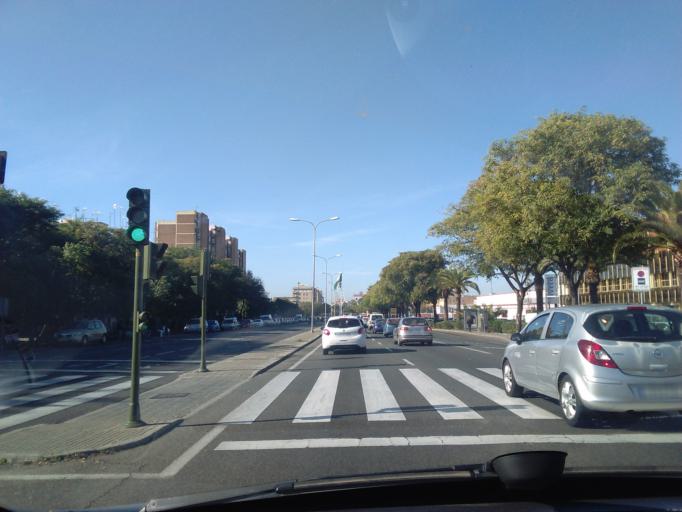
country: ES
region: Andalusia
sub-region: Provincia de Sevilla
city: Sevilla
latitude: 37.3872
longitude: -5.9544
